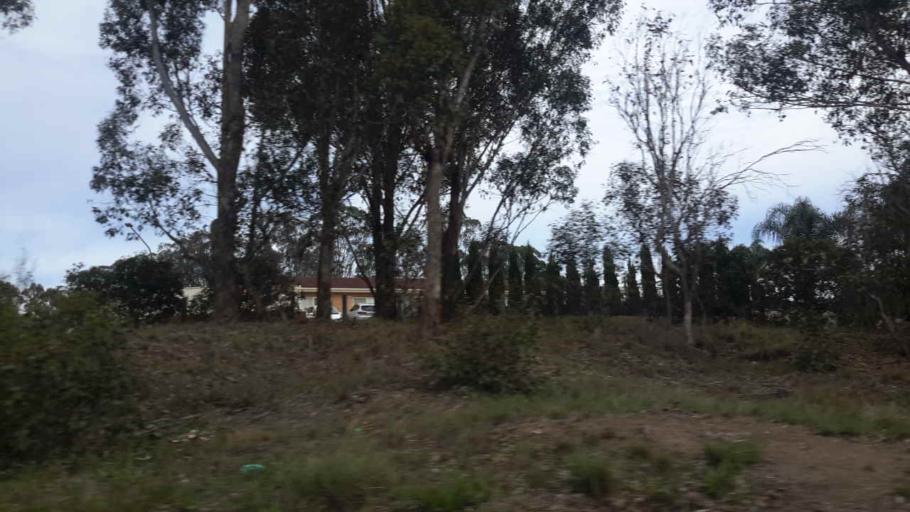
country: AU
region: New South Wales
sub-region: Penrith Municipality
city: Werrington Downs
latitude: -33.7201
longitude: 150.7242
